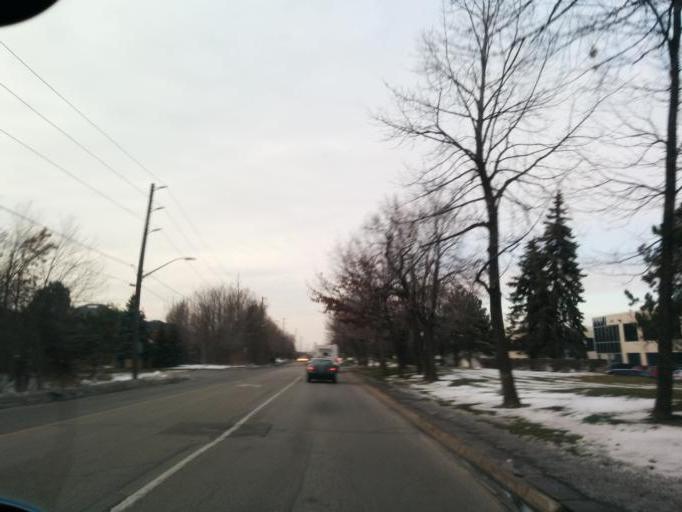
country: CA
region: Ontario
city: Mississauga
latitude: 43.6102
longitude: -79.6811
